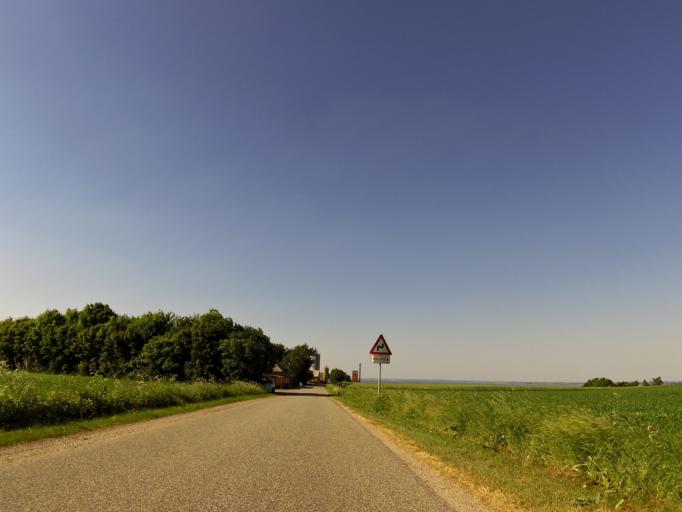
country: DK
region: Central Jutland
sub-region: Holstebro Kommune
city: Vinderup
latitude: 56.4527
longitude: 8.6909
